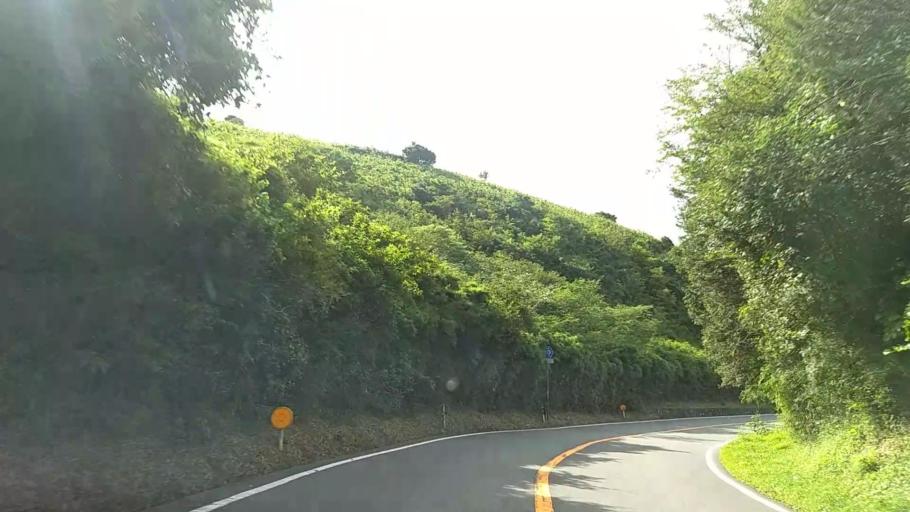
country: JP
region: Kanagawa
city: Yugawara
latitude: 35.1333
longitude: 139.0392
